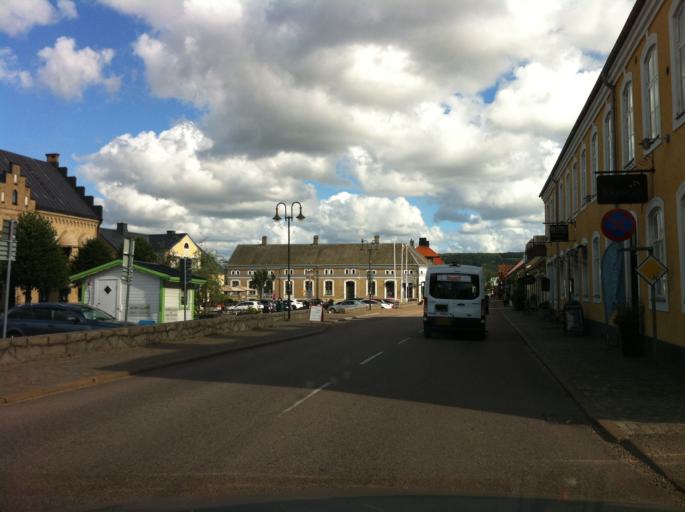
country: SE
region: Skane
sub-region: Bastads Kommun
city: Bastad
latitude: 56.4385
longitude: 12.8070
